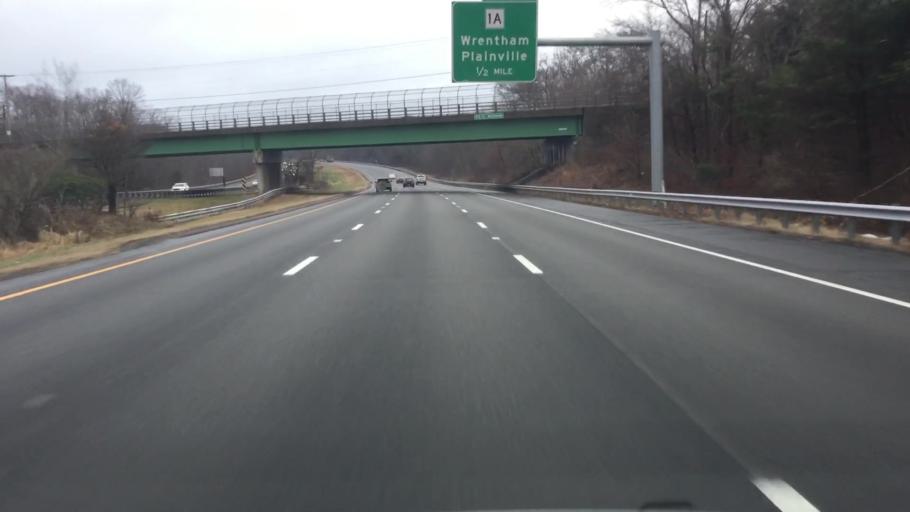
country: US
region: Massachusetts
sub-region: Norfolk County
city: Wrentham
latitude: 42.0443
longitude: -71.3582
